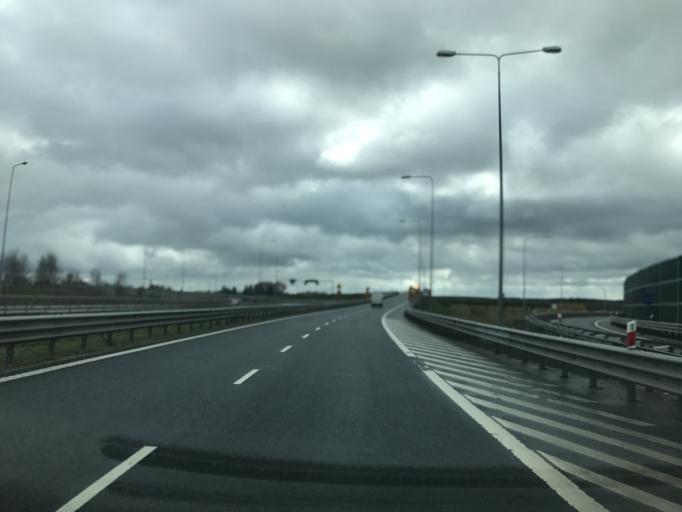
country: PL
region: Warmian-Masurian Voivodeship
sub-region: Powiat olsztynski
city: Olsztynek
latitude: 53.5854
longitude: 20.2546
